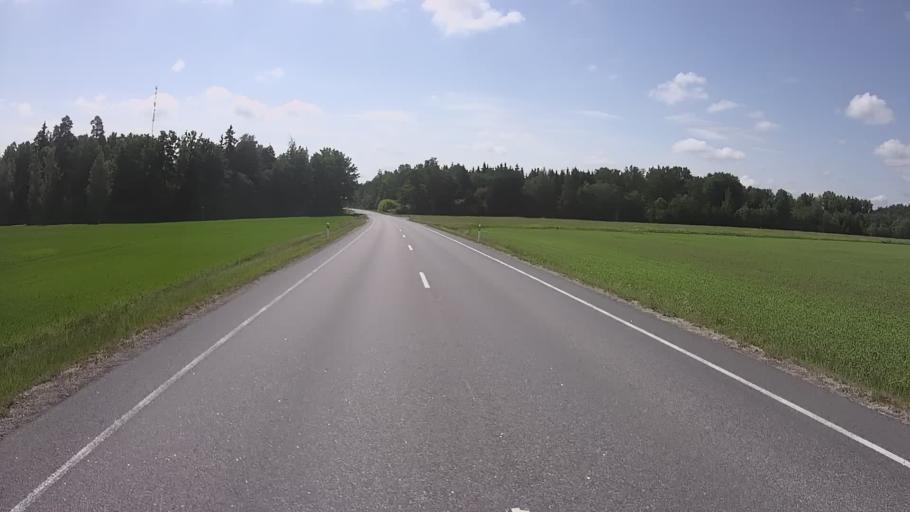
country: EE
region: Tartu
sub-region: Tartu linn
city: Tartu
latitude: 58.3750
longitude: 26.8840
